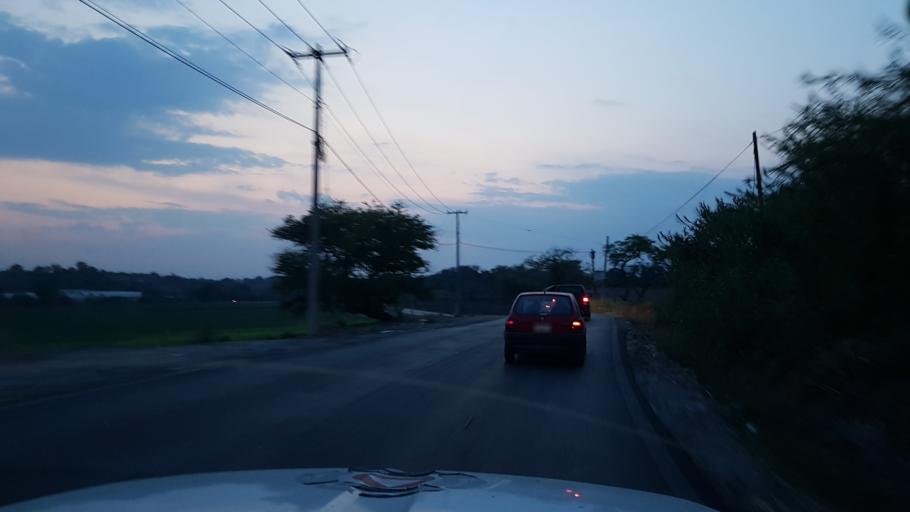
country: MX
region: Morelos
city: Tlaltizapan
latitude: 18.6891
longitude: -99.1341
